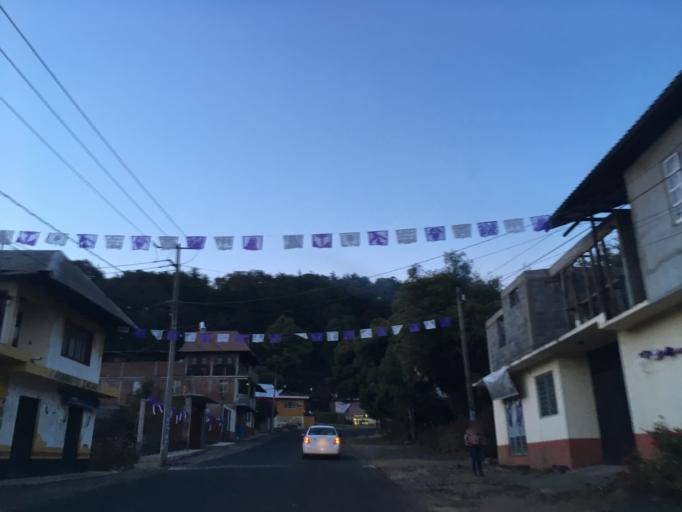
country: MX
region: Michoacan
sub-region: Uruapan
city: Santa Ana Zirosto
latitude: 19.5633
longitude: -102.2908
